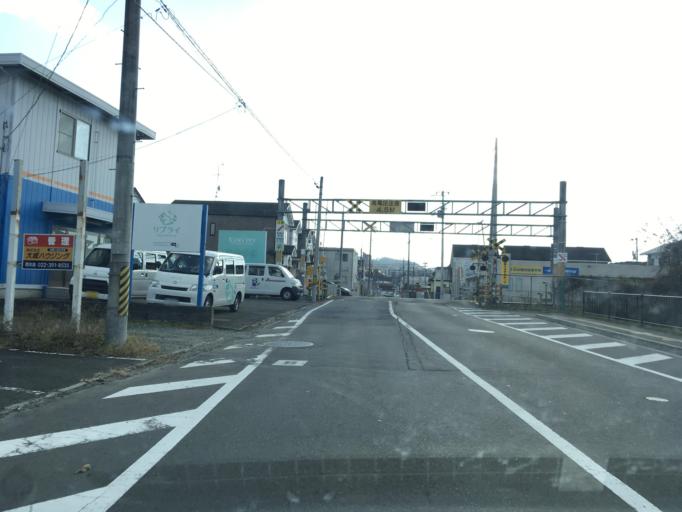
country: JP
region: Miyagi
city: Sendai
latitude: 38.2731
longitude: 140.7645
